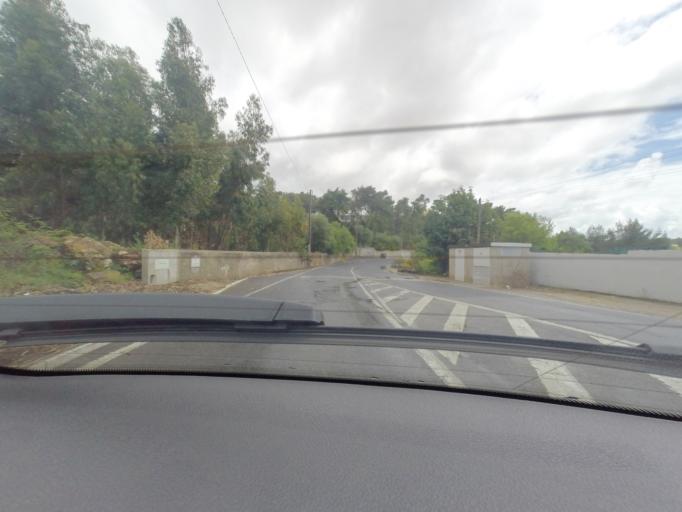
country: PT
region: Lisbon
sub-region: Cascais
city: Parede
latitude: 38.7132
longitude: -9.3702
